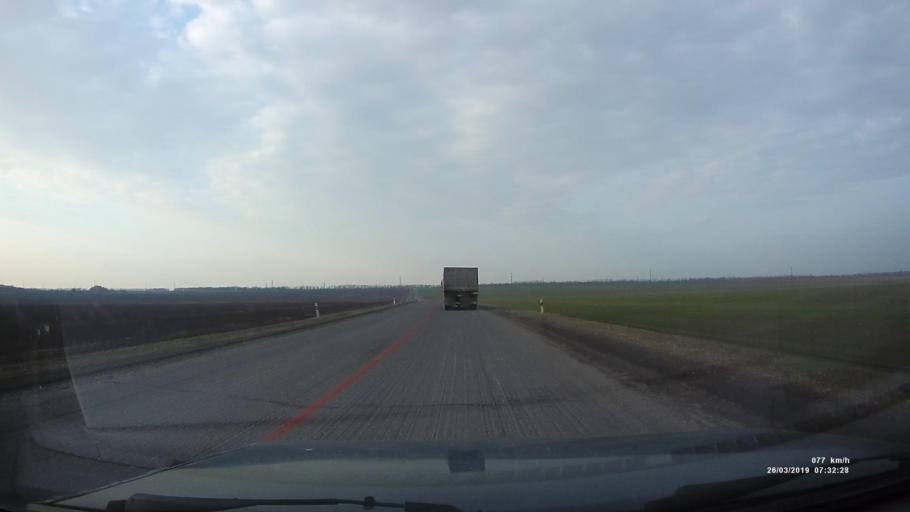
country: RU
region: Rostov
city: Novobessergenovka
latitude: 47.2253
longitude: 38.7775
